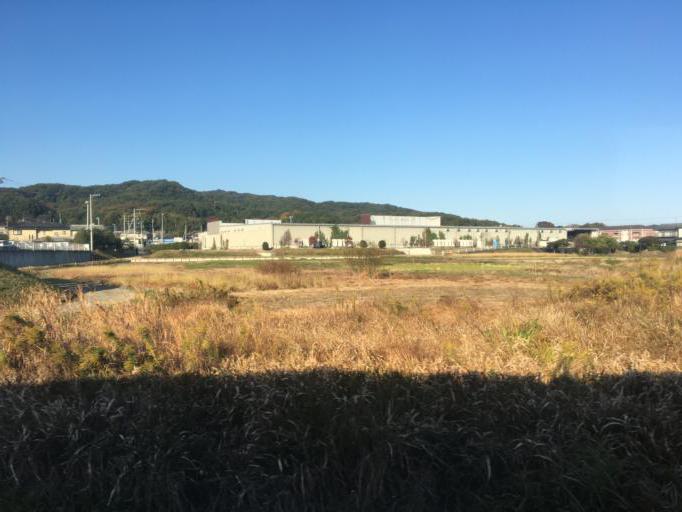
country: JP
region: Saitama
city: Yorii
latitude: 36.1325
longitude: 139.2057
